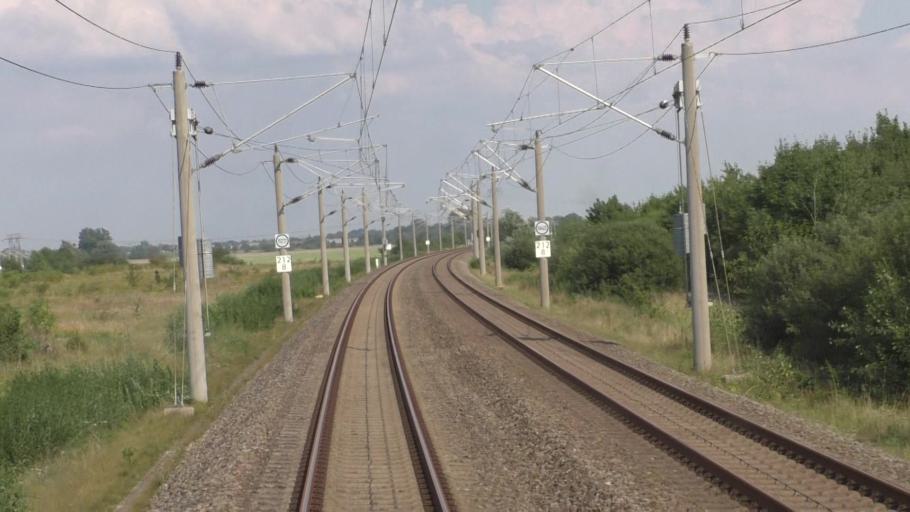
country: DE
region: Saxony-Anhalt
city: Uenglingen
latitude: 52.5817
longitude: 11.7513
